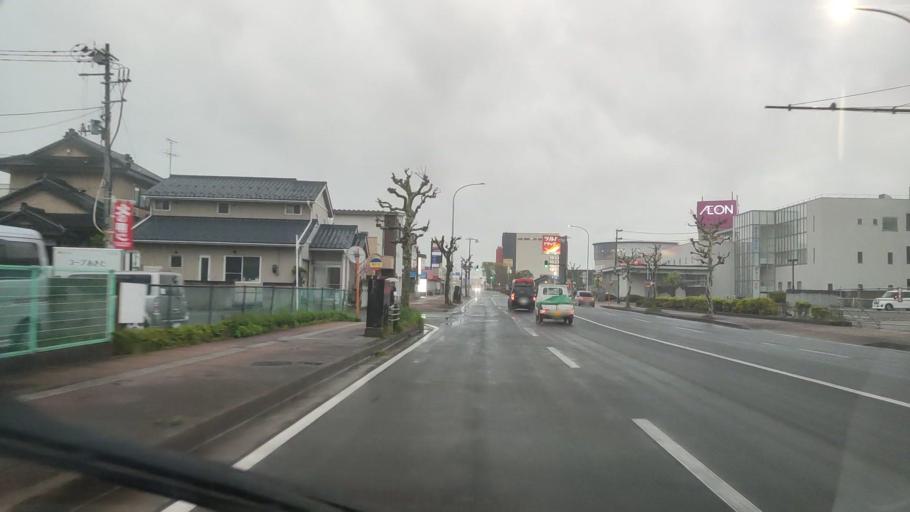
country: JP
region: Akita
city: Akita
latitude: 39.7056
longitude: 140.1121
